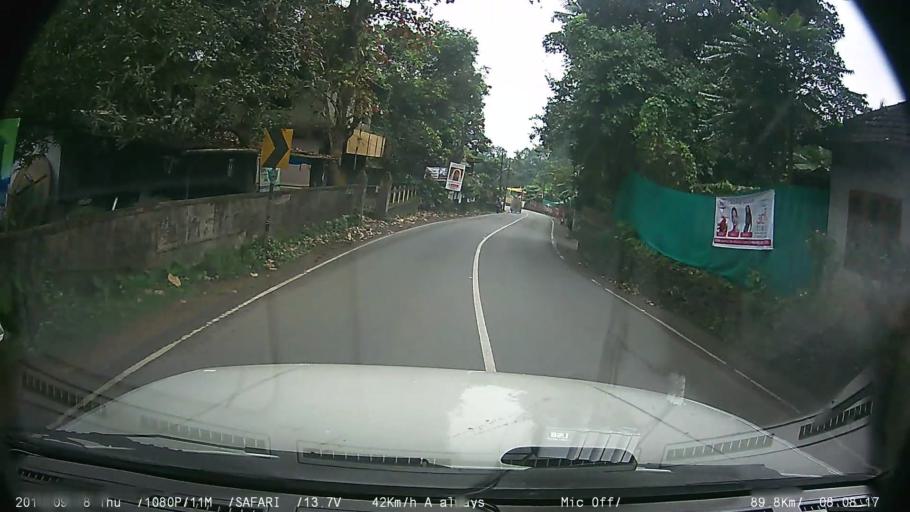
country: IN
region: Kerala
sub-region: Kottayam
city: Kottayam
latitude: 9.5946
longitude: 76.5848
